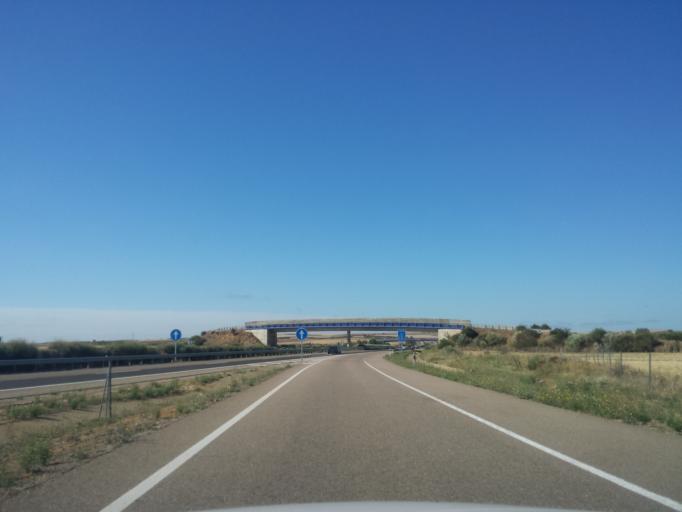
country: ES
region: Castille and Leon
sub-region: Provincia de Zamora
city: Matilla de Arzon
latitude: 42.1247
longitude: -5.6513
